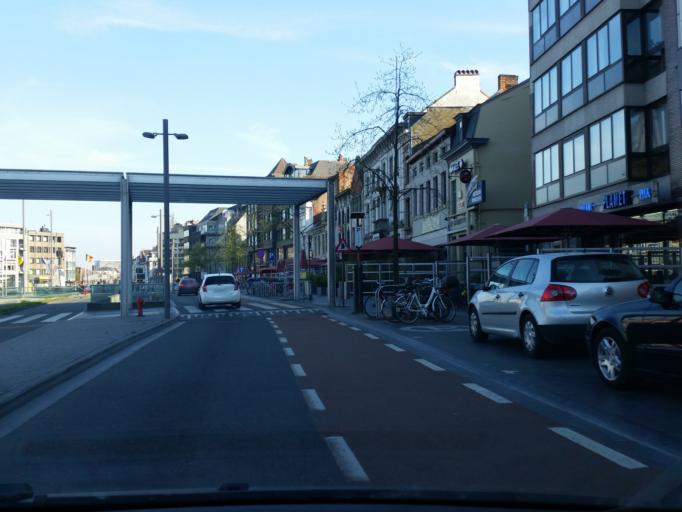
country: BE
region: Flanders
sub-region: Provincie Oost-Vlaanderen
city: Sint-Niklaas
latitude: 51.1642
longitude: 4.1393
